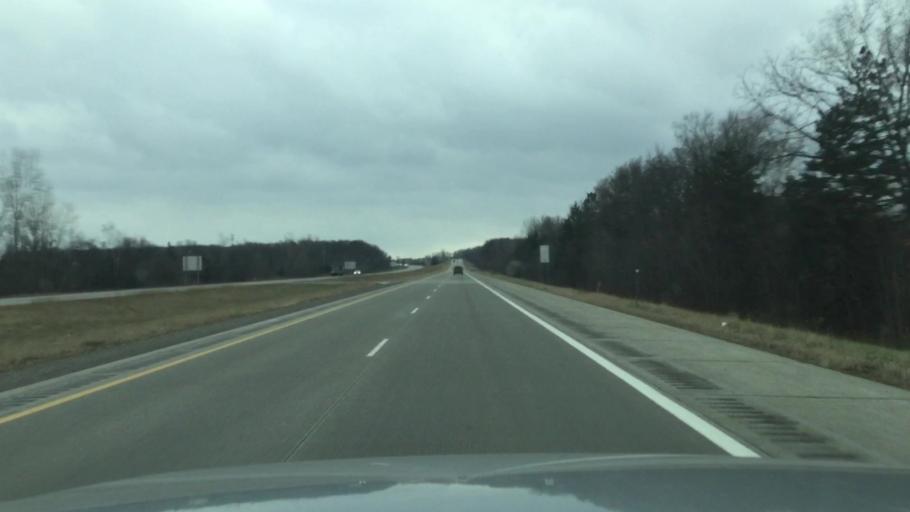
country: US
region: Michigan
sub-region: Genesee County
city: Grand Blanc
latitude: 42.9333
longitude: -83.6814
